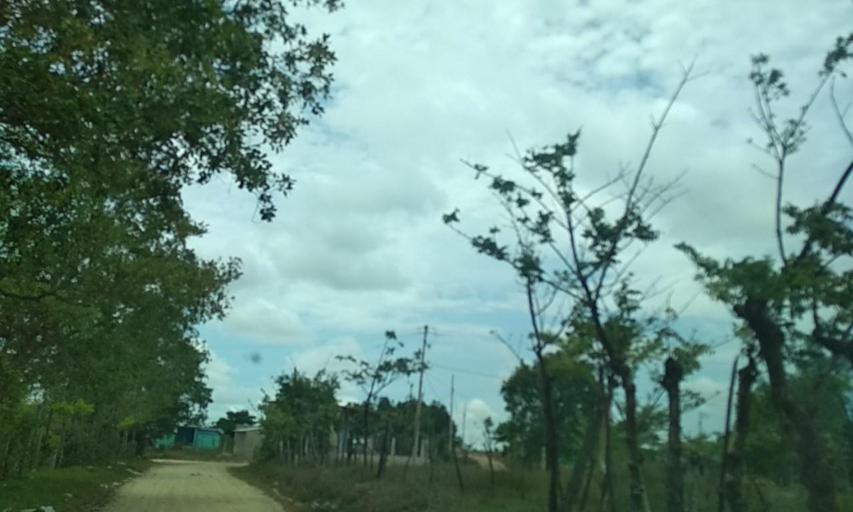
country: MX
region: Veracruz
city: Las Choapas
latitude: 17.8977
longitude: -94.1191
